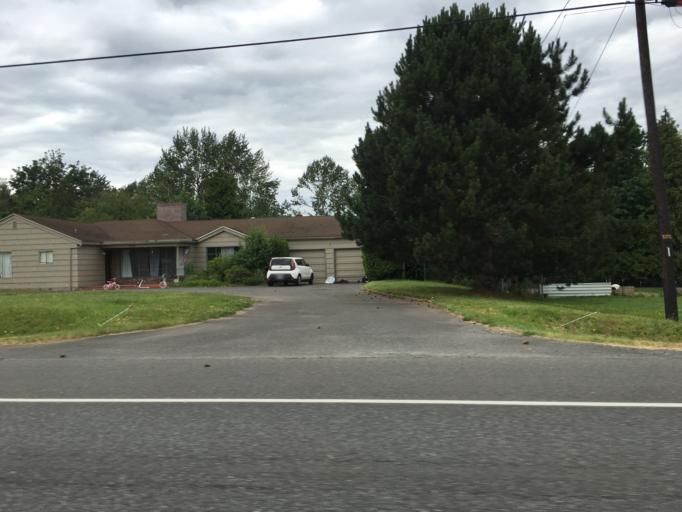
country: US
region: Washington
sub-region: Whatcom County
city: Bellingham
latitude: 48.8241
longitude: -122.4861
